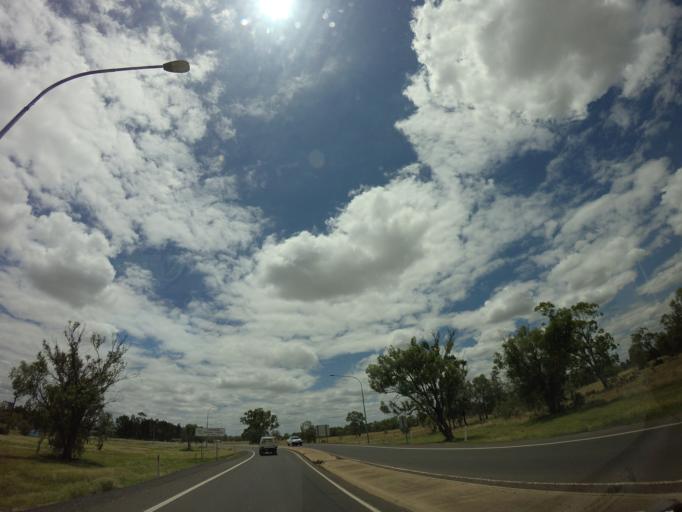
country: AU
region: Queensland
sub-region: Goondiwindi
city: Goondiwindi
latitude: -28.5533
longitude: 150.3218
